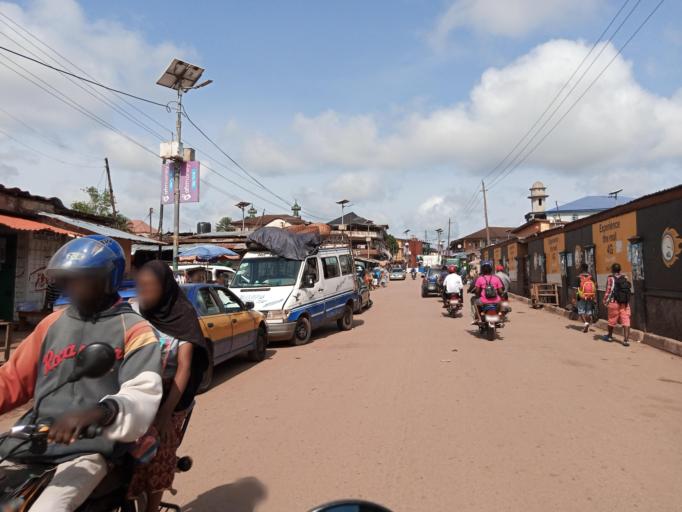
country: SL
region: Southern Province
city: Bo
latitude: 7.9654
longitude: -11.7372
